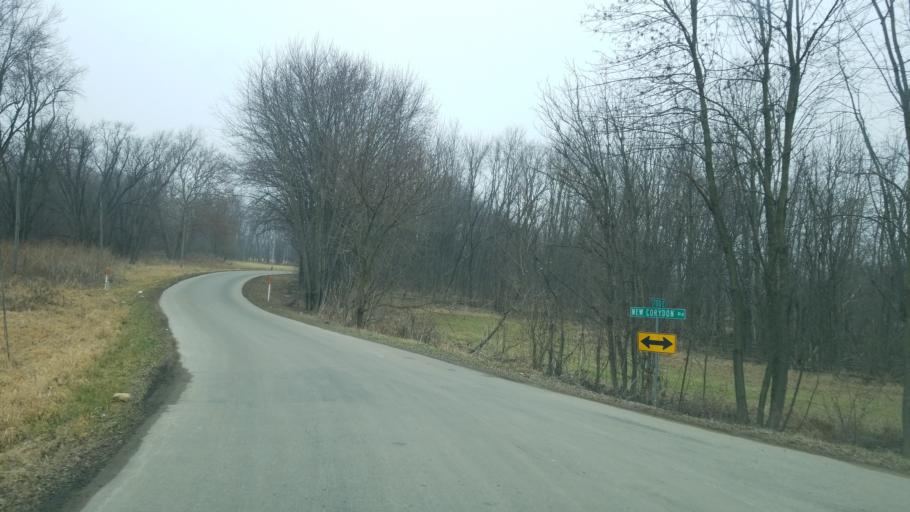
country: US
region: Indiana
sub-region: Adams County
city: Geneva
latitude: 40.5684
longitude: -84.8486
